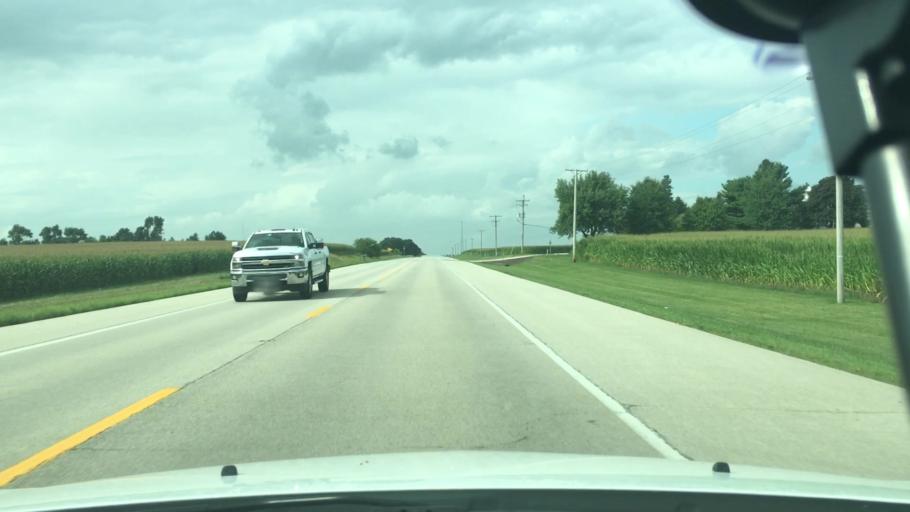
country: US
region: Illinois
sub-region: DeKalb County
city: Waterman
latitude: 41.7792
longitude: -88.7542
